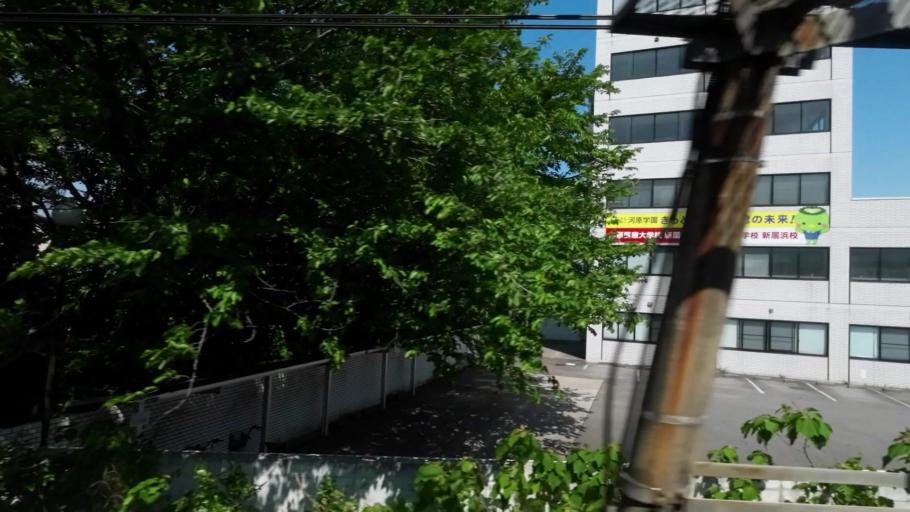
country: JP
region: Ehime
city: Niihama
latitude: 33.9447
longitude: 133.2910
